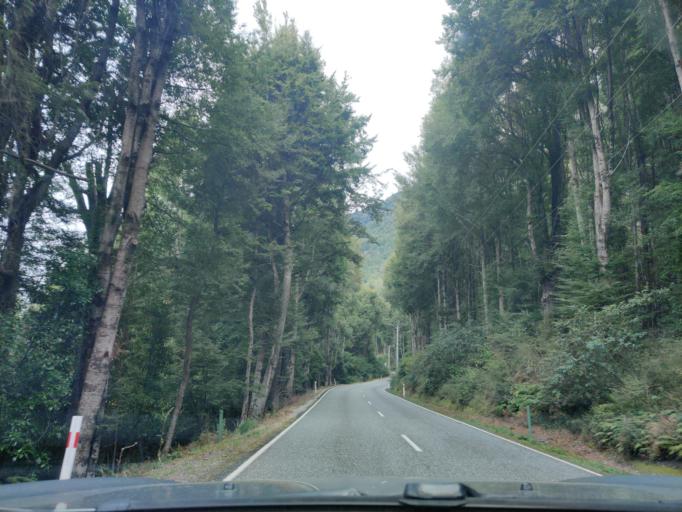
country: NZ
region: Otago
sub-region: Queenstown-Lakes District
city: Queenstown
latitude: -45.0700
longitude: 168.5050
